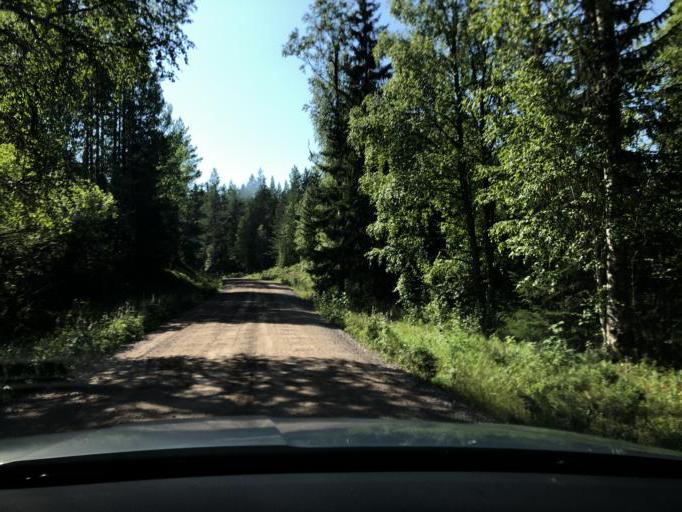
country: SE
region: Dalarna
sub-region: Orsa Kommun
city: Orsa
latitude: 61.2669
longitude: 14.7459
